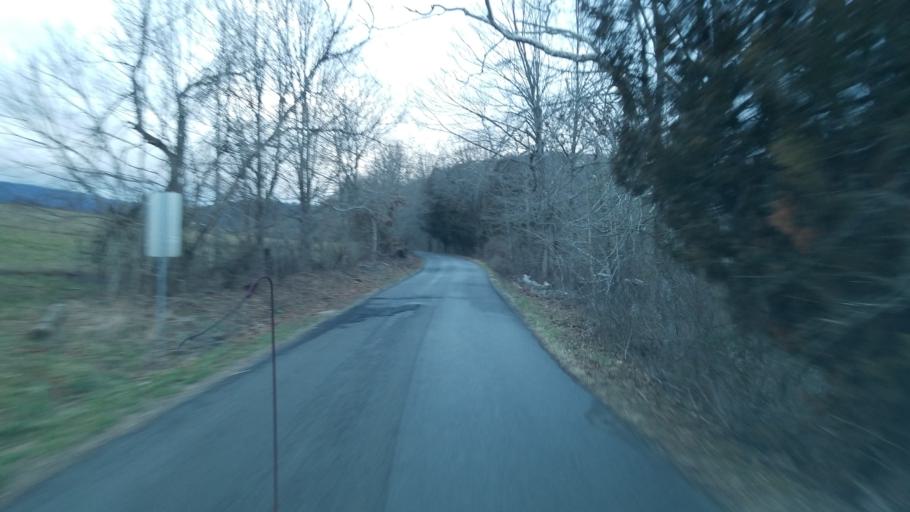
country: US
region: Virginia
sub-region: Pulaski County
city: Pulaski
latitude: 37.1618
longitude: -80.8614
